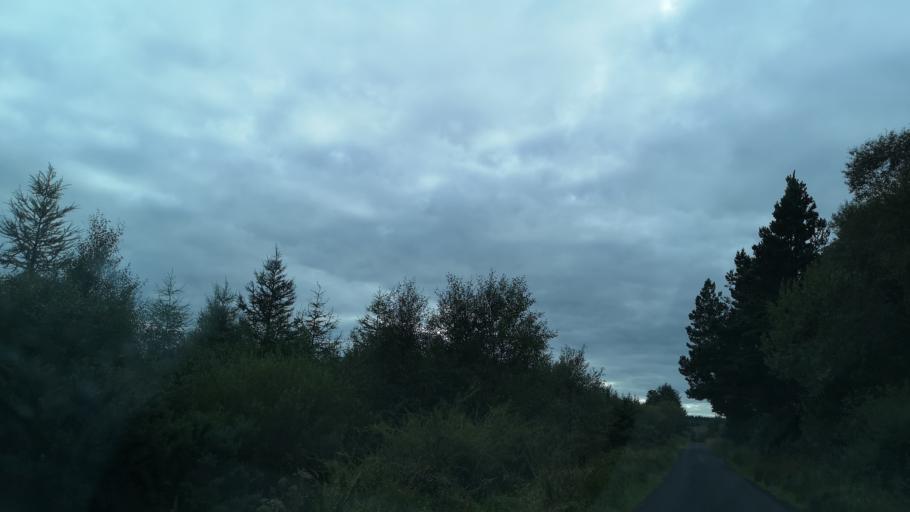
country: IE
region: Connaught
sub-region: County Galway
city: Loughrea
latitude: 53.1315
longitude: -8.5147
